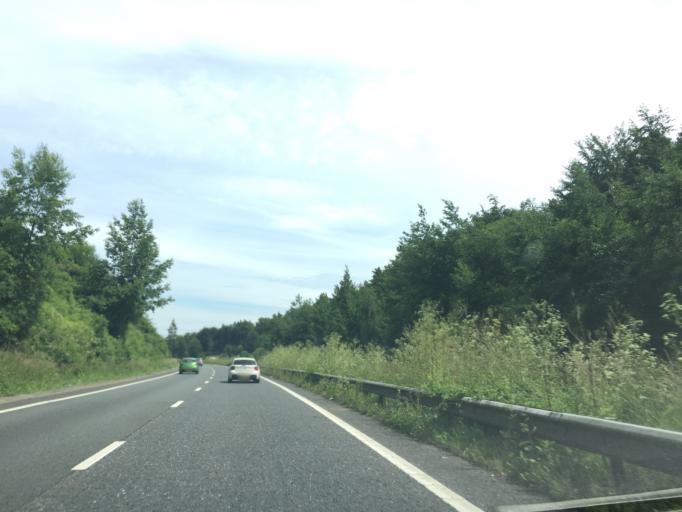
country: GB
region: England
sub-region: Kent
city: Canterbury
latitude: 51.2544
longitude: 1.0884
